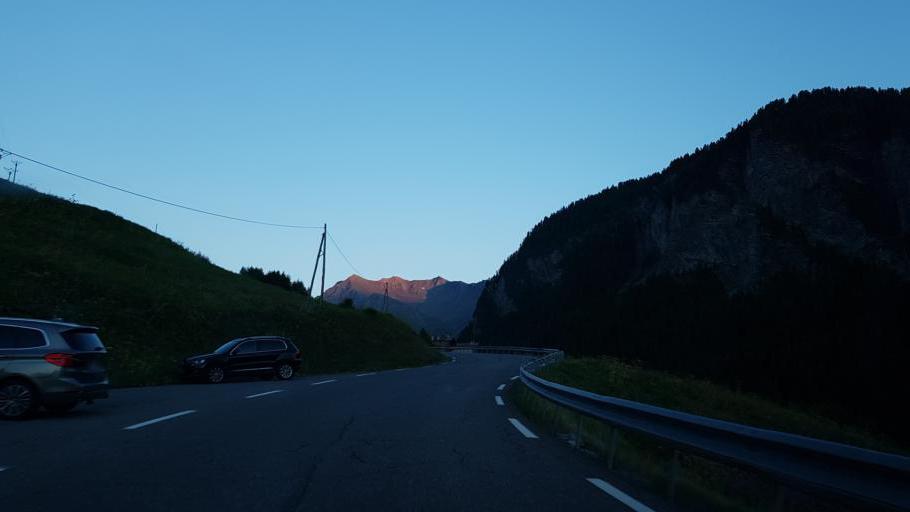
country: IT
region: Piedmont
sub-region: Provincia di Cuneo
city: Pontechianale
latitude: 44.7014
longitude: 6.8592
